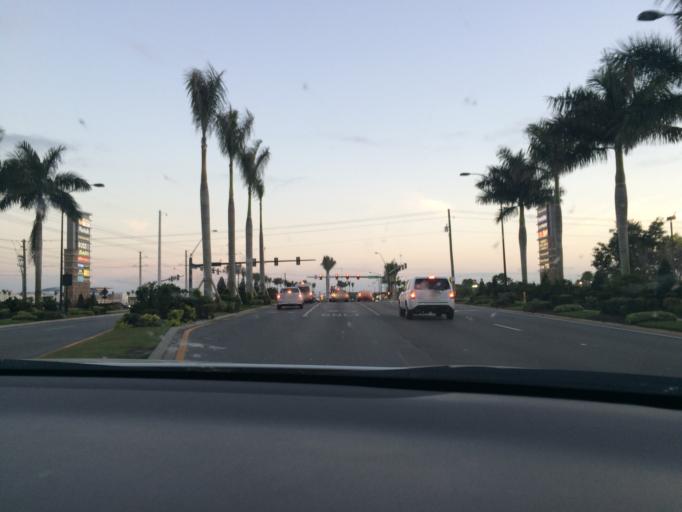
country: US
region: Florida
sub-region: Sarasota County
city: The Meadows
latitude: 27.3897
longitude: -82.4558
